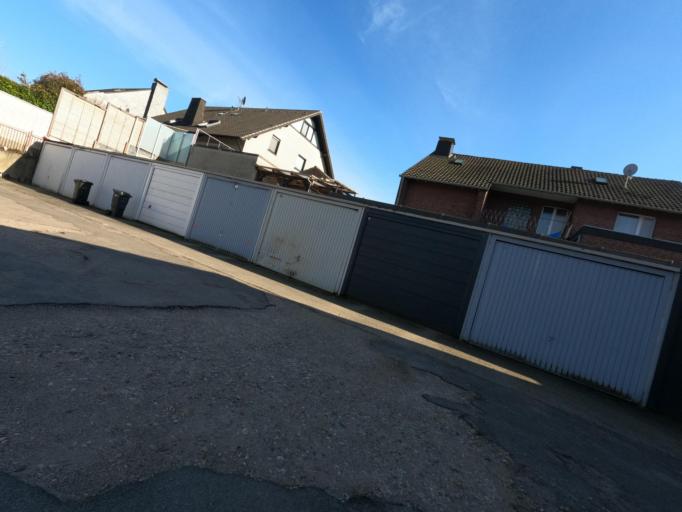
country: DE
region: North Rhine-Westphalia
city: Huckelhoven
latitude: 51.0627
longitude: 6.2201
